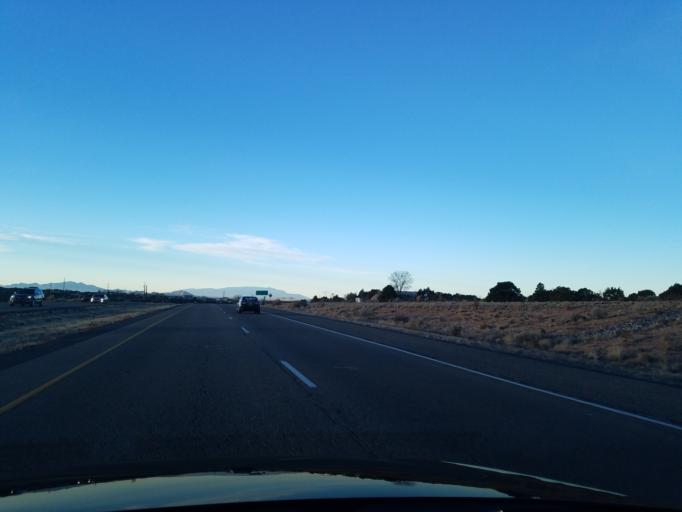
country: US
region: New Mexico
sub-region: Santa Fe County
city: Agua Fria
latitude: 35.6736
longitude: -106.0152
